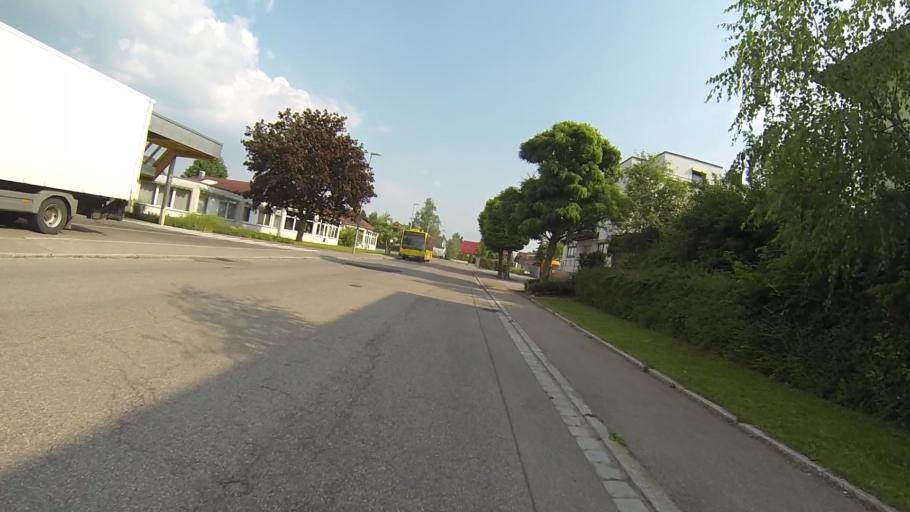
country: DE
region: Baden-Wuerttemberg
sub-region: Tuebingen Region
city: Beimerstetten
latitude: 48.4478
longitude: 9.9843
